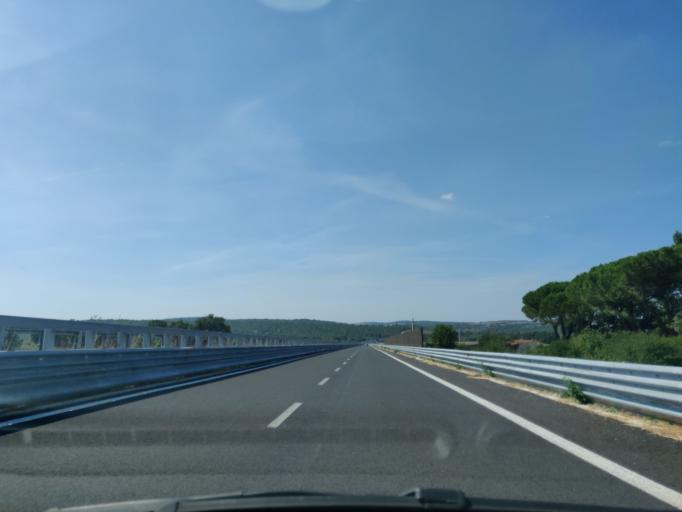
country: IT
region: Latium
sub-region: Provincia di Viterbo
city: Blera
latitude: 42.3011
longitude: 11.9768
